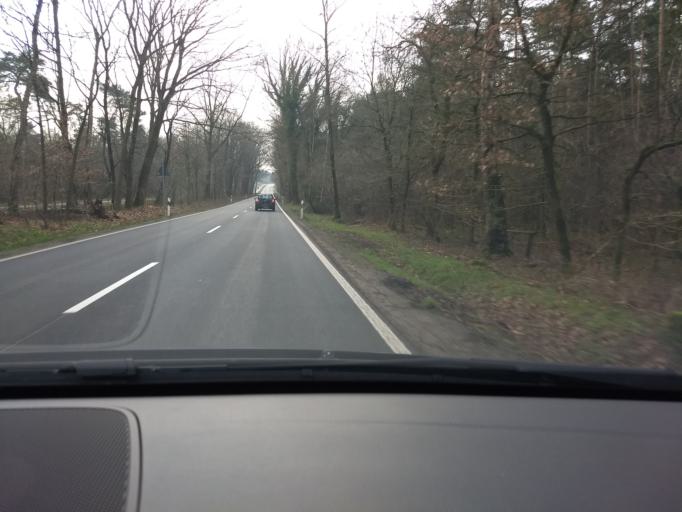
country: DE
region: North Rhine-Westphalia
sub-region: Regierungsbezirk Munster
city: Heiden
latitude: 51.8583
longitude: 6.9195
